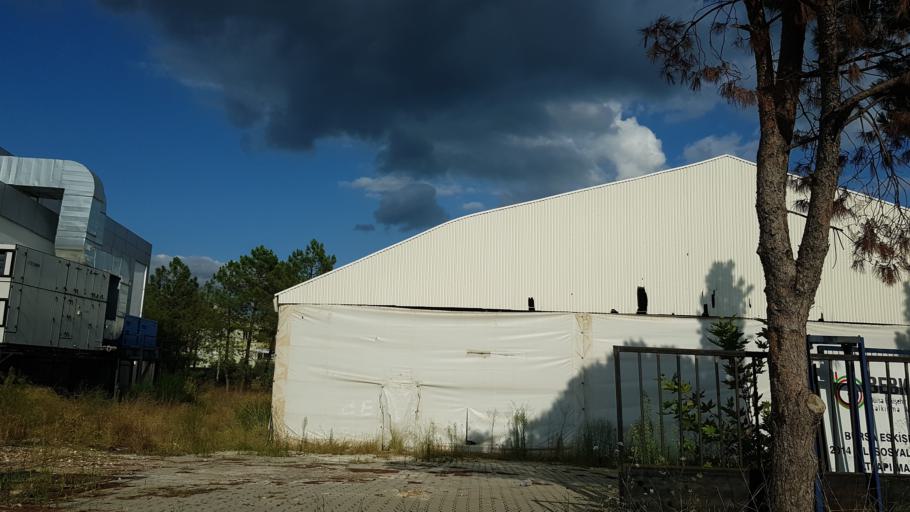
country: TR
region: Bursa
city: Orhangazi
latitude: 40.5036
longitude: 29.3164
